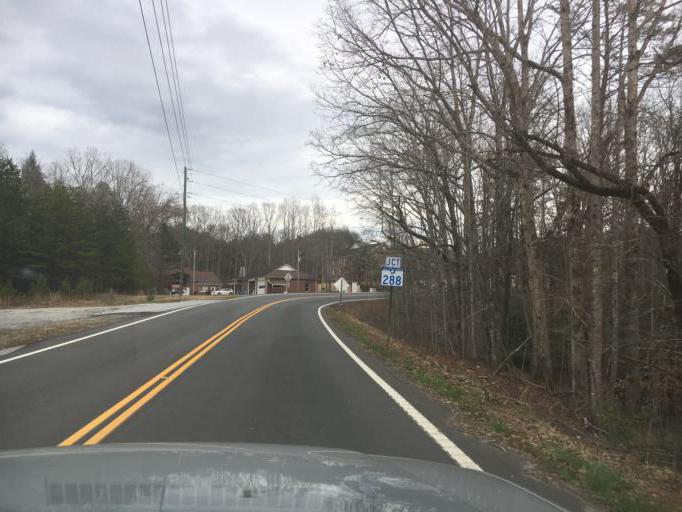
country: US
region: South Carolina
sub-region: Pickens County
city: Pickens
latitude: 34.9892
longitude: -82.7556
